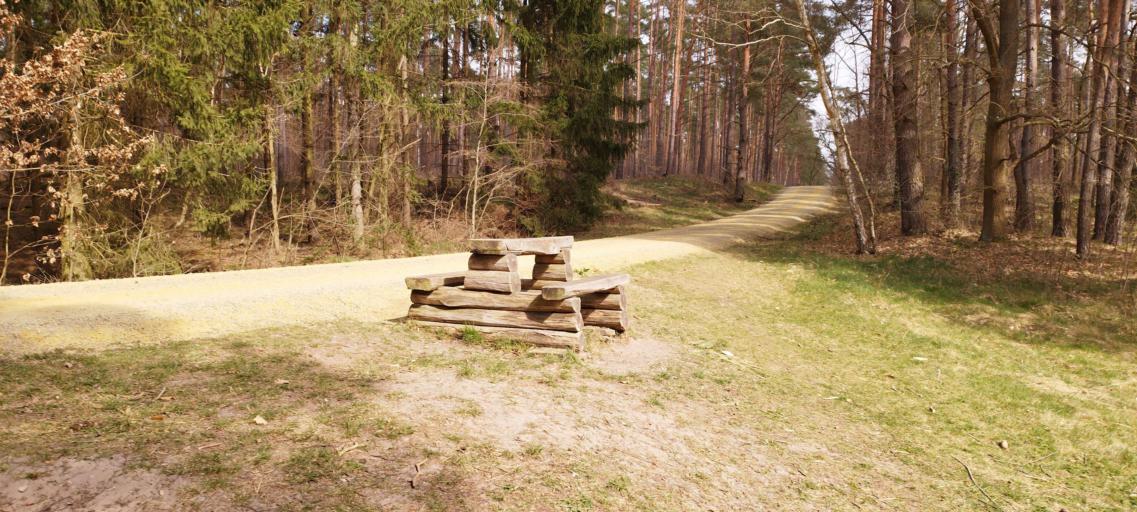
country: DE
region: Brandenburg
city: Grunheide
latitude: 52.4140
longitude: 13.8548
